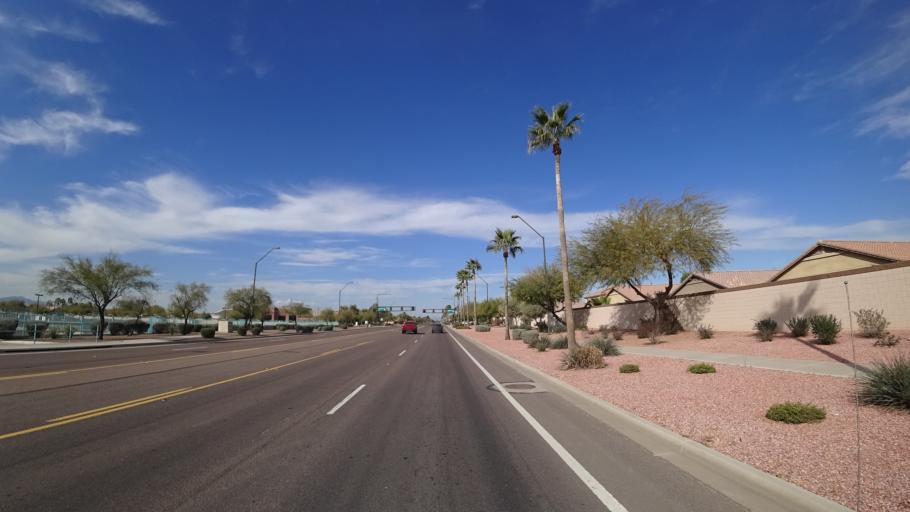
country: US
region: Arizona
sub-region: Maricopa County
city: Avondale
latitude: 33.4267
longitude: -112.3063
